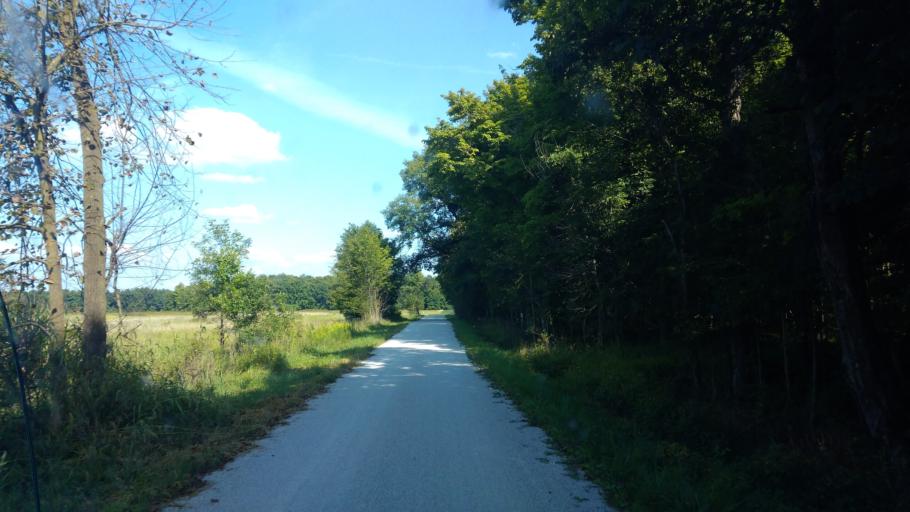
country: US
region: Ohio
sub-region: Hardin County
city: Kenton
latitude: 40.6294
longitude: -83.4419
